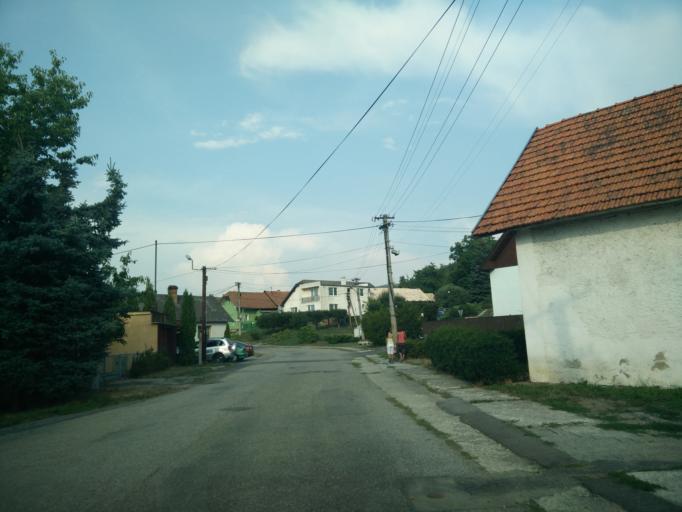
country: SK
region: Banskobystricky
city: Ziar nad Hronom
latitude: 48.5428
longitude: 18.8065
